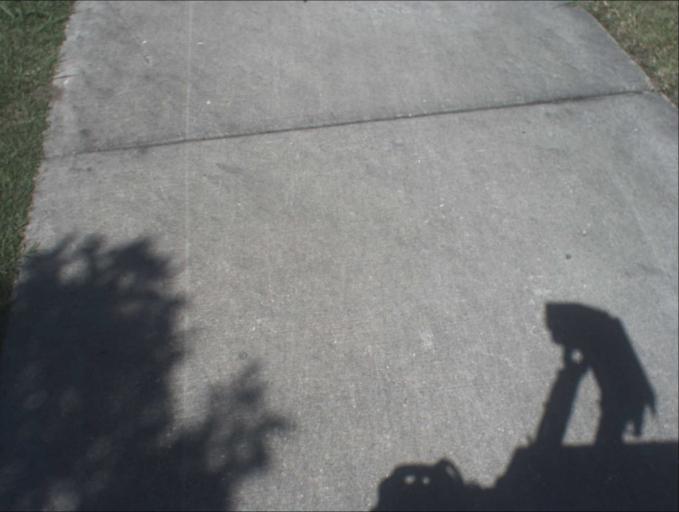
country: AU
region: Queensland
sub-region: Logan
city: Windaroo
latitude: -27.7217
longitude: 153.1714
